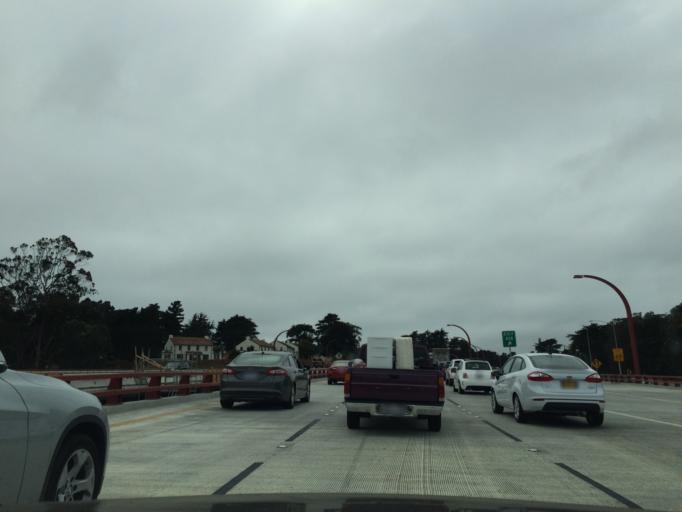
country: US
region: California
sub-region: San Francisco County
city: San Francisco
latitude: 37.8029
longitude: -122.4682
